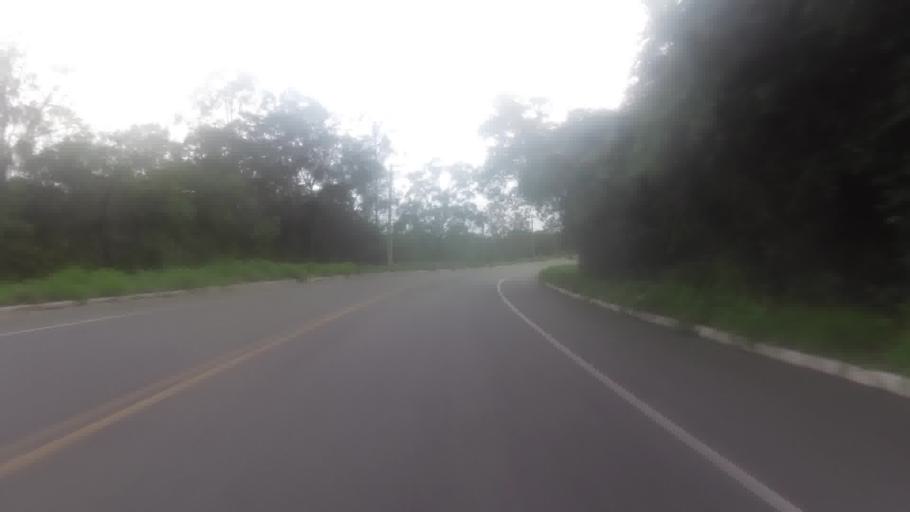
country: BR
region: Espirito Santo
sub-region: Piuma
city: Piuma
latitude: -20.7993
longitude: -40.6260
